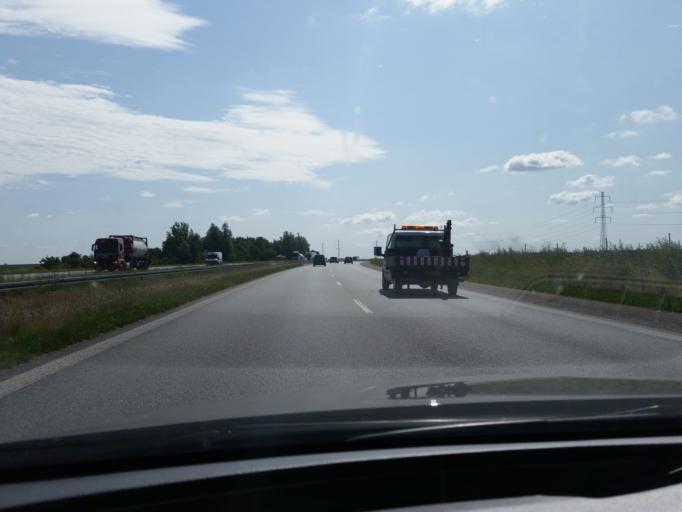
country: DK
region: Zealand
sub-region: Ringsted Kommune
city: Ringsted
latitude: 55.4557
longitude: 11.8395
